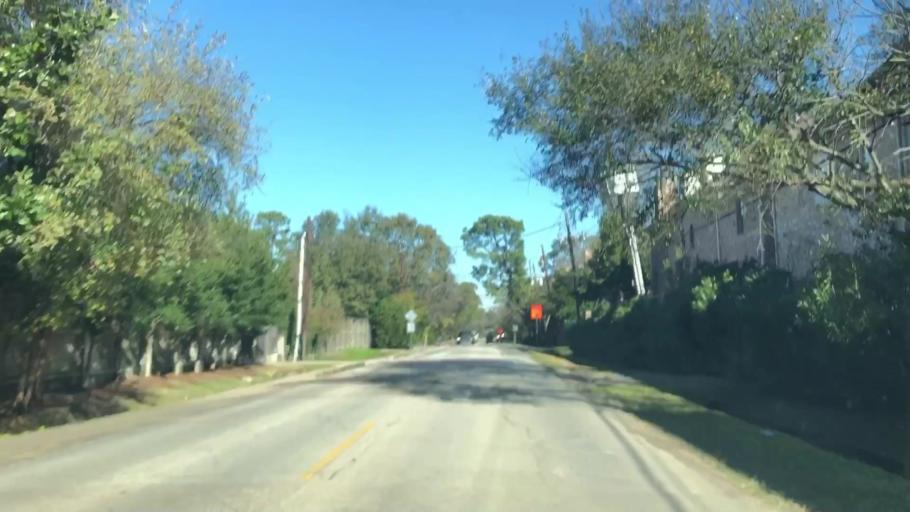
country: US
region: Texas
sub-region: Harris County
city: Hunters Creek Village
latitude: 29.7560
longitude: -95.4675
